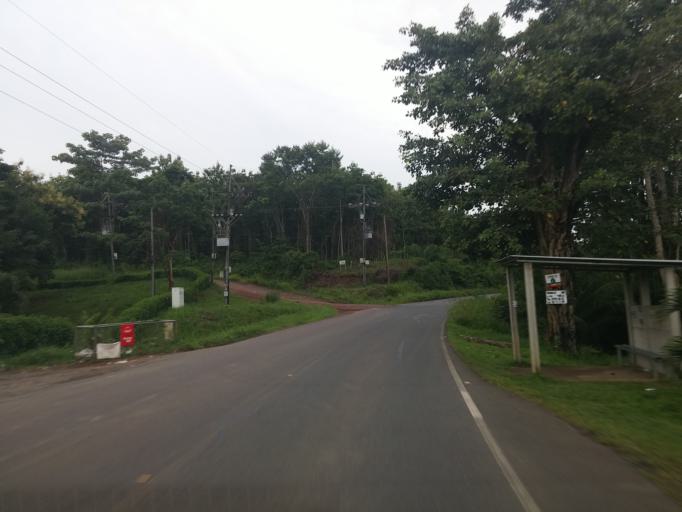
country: CR
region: Alajuela
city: Upala
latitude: 10.8366
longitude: -85.0224
